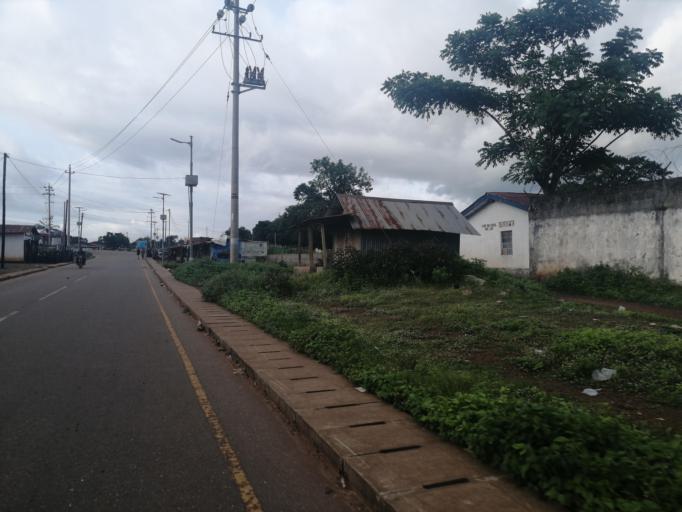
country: SL
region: Northern Province
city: Port Loko
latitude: 8.7735
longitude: -12.7879
